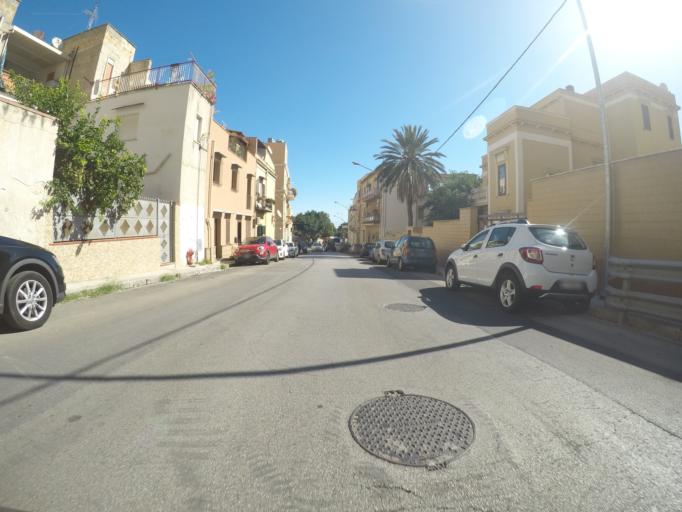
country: IT
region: Sicily
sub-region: Palermo
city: Palermo
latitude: 38.1654
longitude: 13.3665
